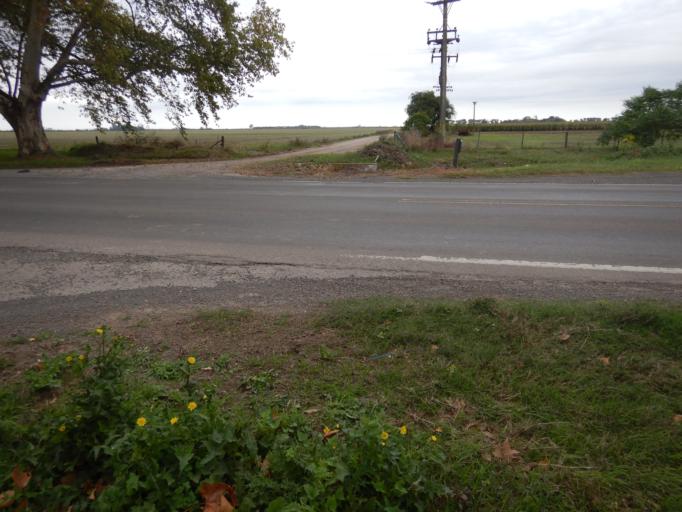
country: AR
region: Santa Fe
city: Carcarana
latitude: -32.8761
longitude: -61.0693
